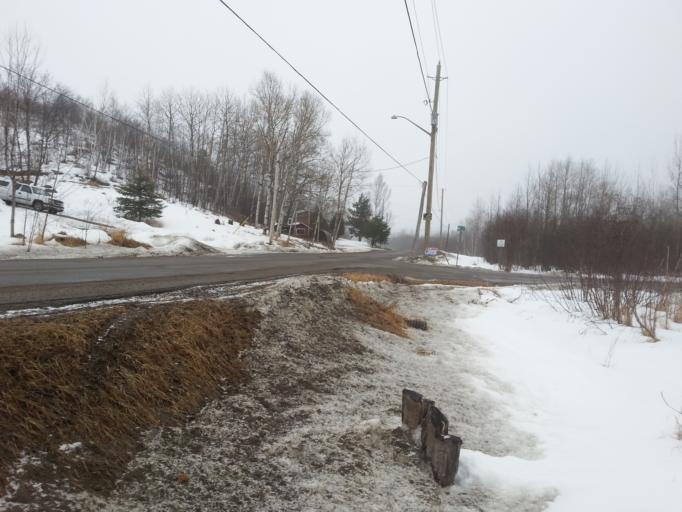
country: CA
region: Ontario
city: Greater Sudbury
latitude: 46.4053
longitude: -80.9861
